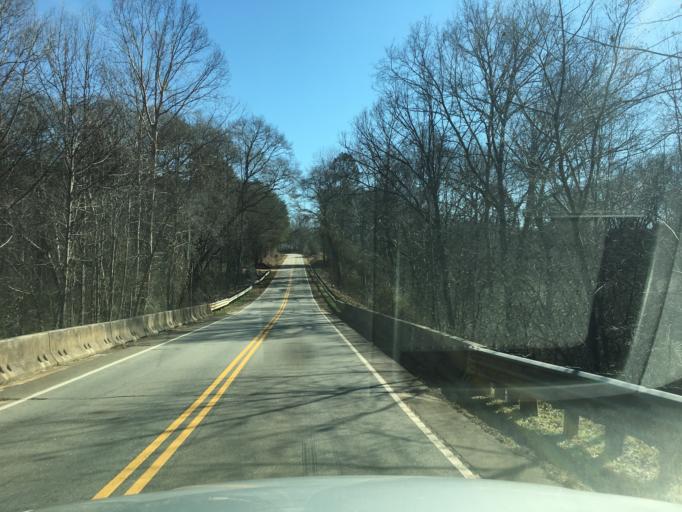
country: US
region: South Carolina
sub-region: Pickens County
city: Liberty
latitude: 34.7947
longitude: -82.7314
